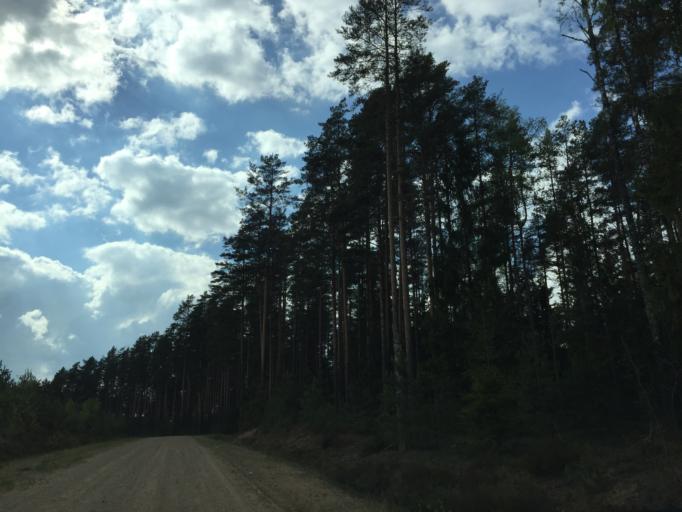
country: LV
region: Sigulda
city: Sigulda
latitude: 57.2971
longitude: 24.8463
